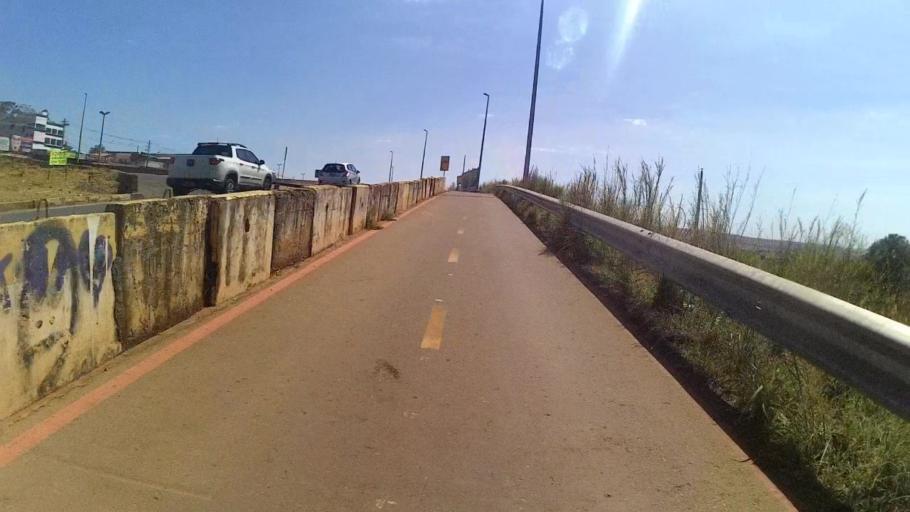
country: BR
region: Federal District
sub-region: Brasilia
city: Brasilia
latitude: -15.6739
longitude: -47.8412
